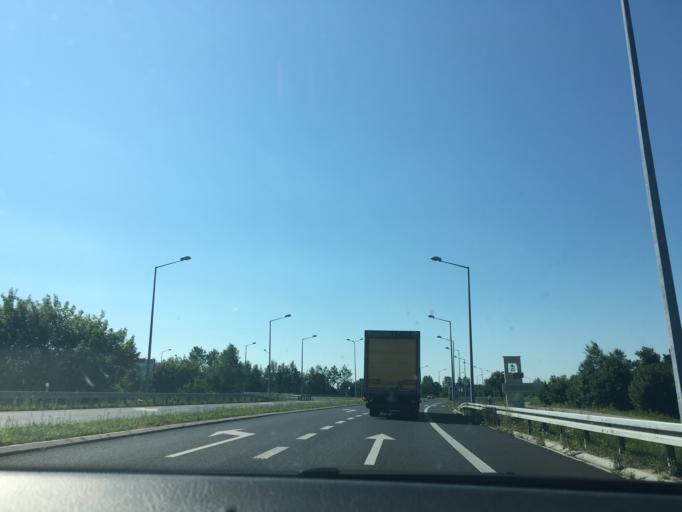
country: PL
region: Lublin Voivodeship
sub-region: Powiat lubartowski
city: Lubartow
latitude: 51.4807
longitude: 22.5889
